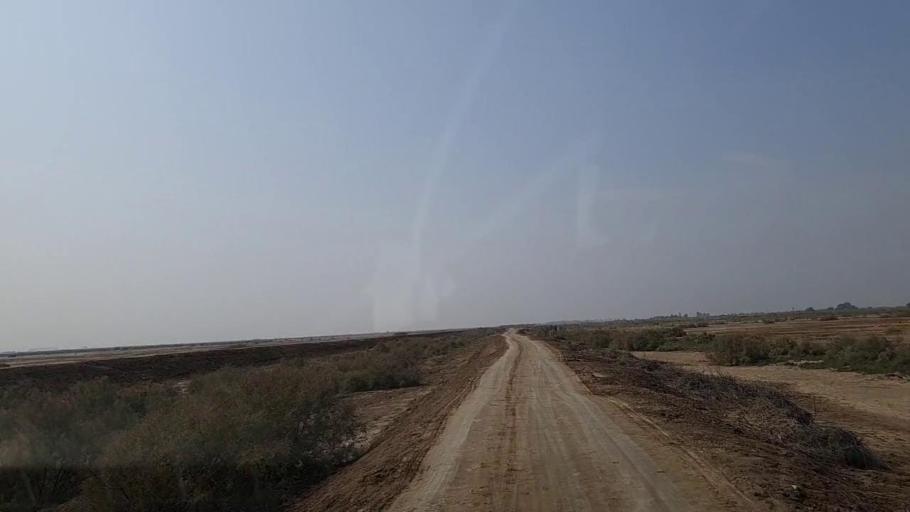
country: PK
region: Sindh
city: Gharo
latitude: 24.6737
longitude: 67.7196
